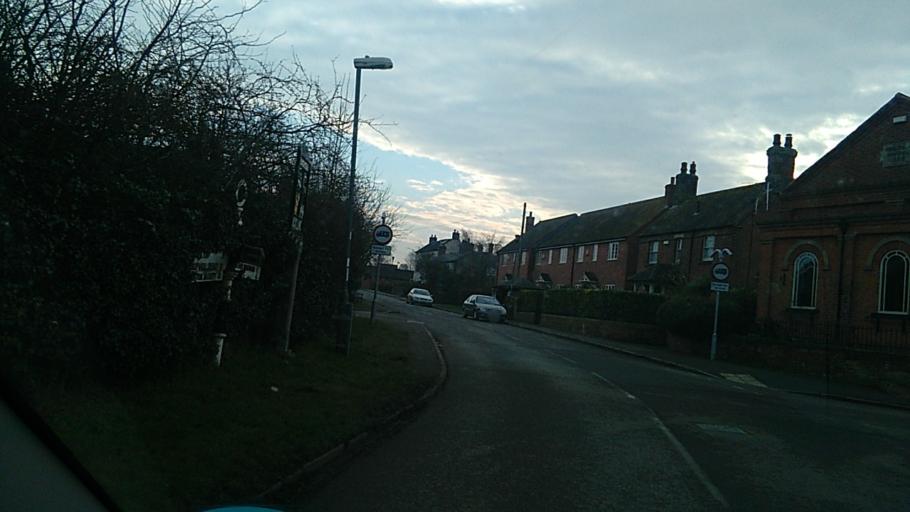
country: GB
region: England
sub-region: Nottinghamshire
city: Cropwell Bishop
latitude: 52.8543
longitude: -0.9752
